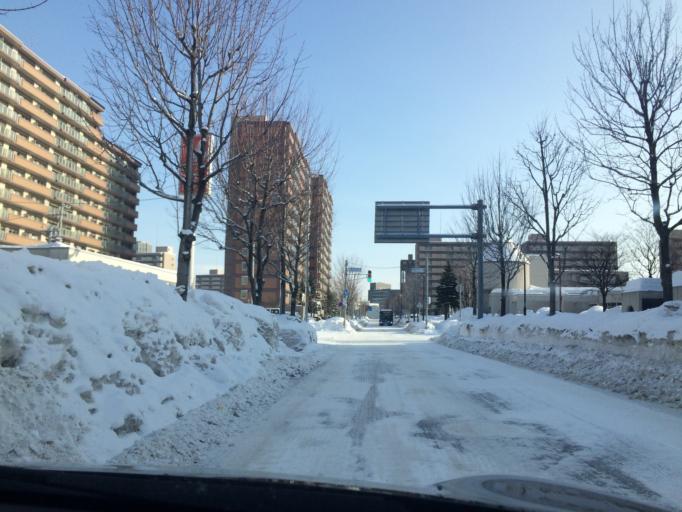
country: JP
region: Hokkaido
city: Ebetsu
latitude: 43.0345
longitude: 141.4661
